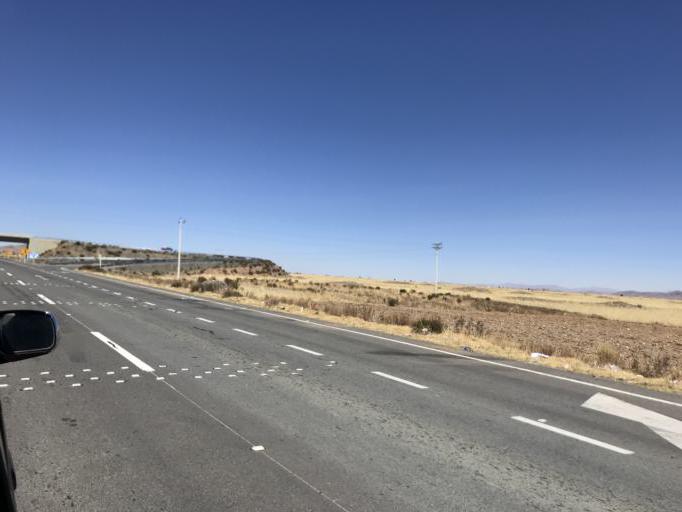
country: BO
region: La Paz
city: Batallas
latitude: -16.3185
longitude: -68.4400
